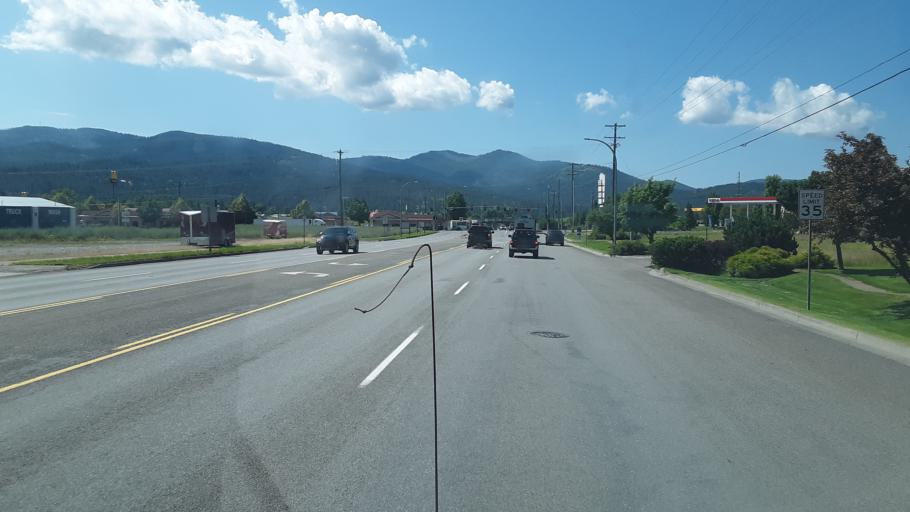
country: US
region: Idaho
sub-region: Kootenai County
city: Post Falls
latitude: 47.7138
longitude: -117.0018
